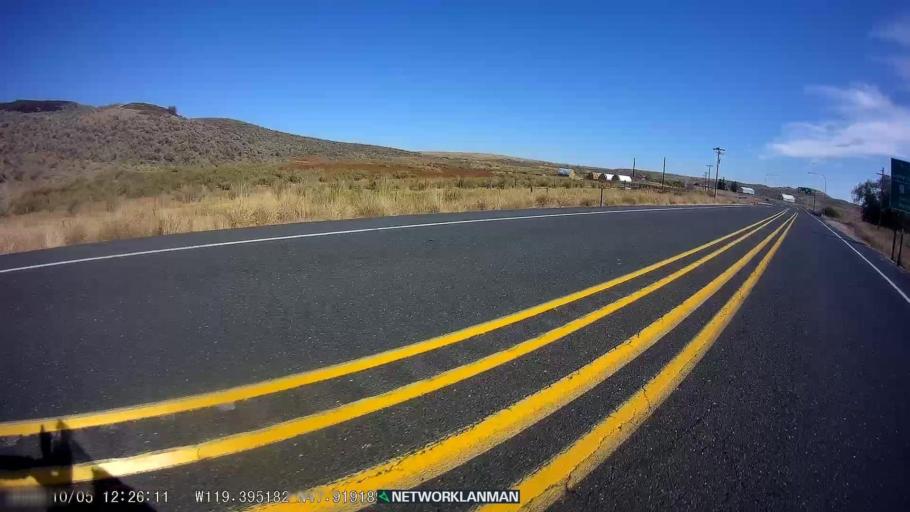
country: US
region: Washington
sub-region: Douglas County
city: Bridgeport
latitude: 47.9192
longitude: -119.3955
